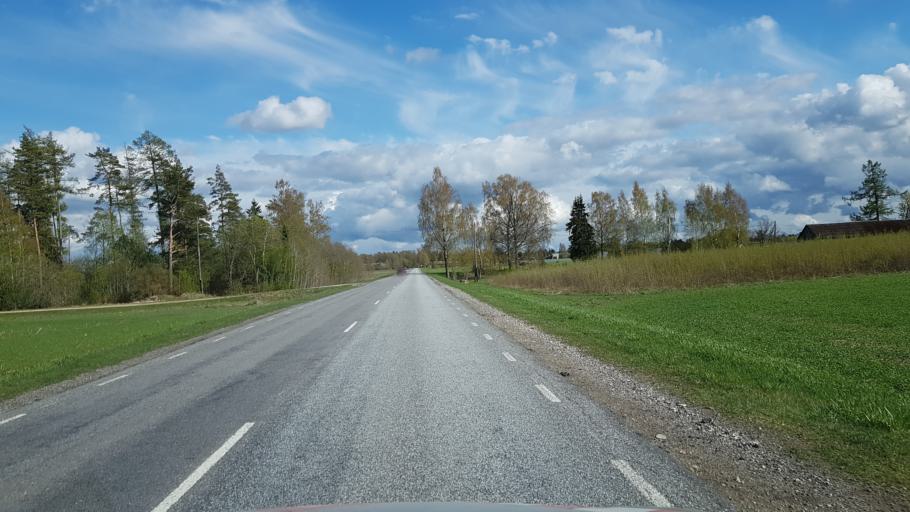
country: EE
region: Laeaene-Virumaa
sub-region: Vaeike-Maarja vald
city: Vaike-Maarja
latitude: 59.1399
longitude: 26.2404
